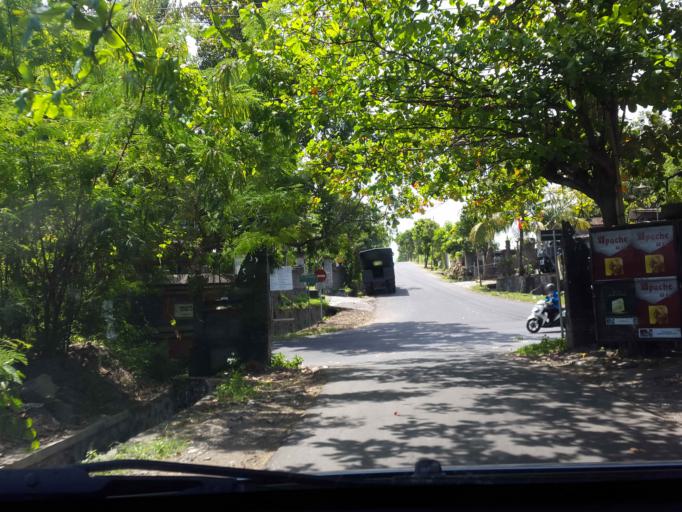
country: ID
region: Bali
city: Semarapura
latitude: -8.5538
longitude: 115.3976
